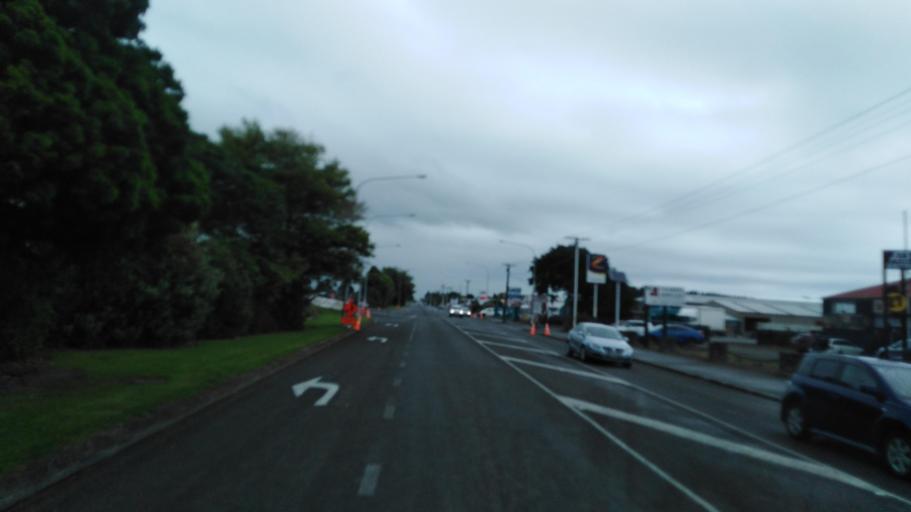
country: NZ
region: Manawatu-Wanganui
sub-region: Horowhenua District
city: Levin
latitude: -40.6355
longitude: 175.2734
